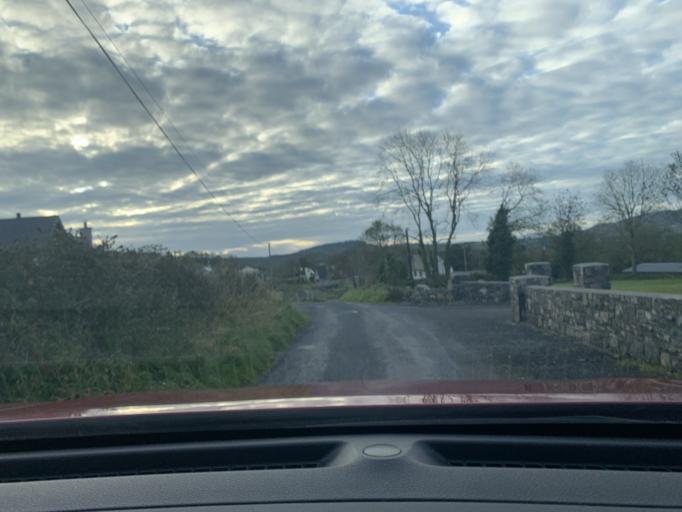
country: IE
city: Ballisodare
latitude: 54.2332
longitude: -8.5159
